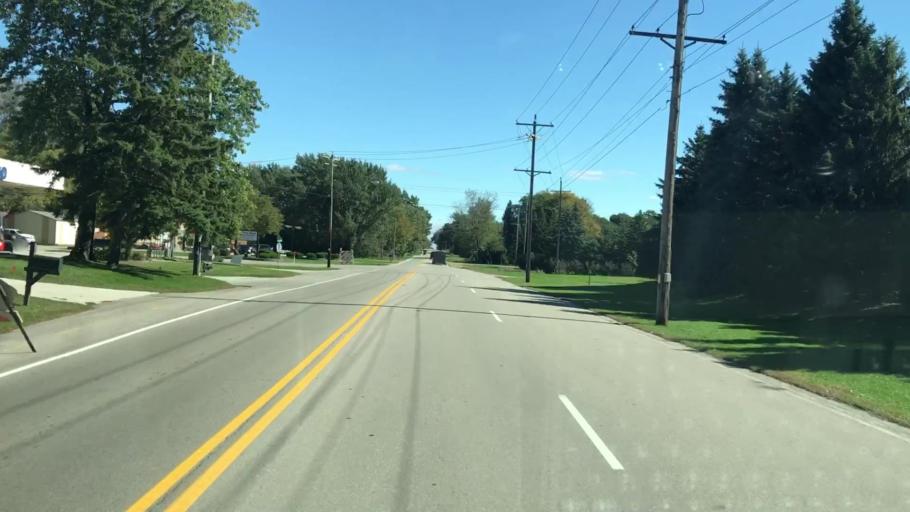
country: US
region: Wisconsin
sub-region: Waukesha County
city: Lannon
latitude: 43.1046
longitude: -88.1365
